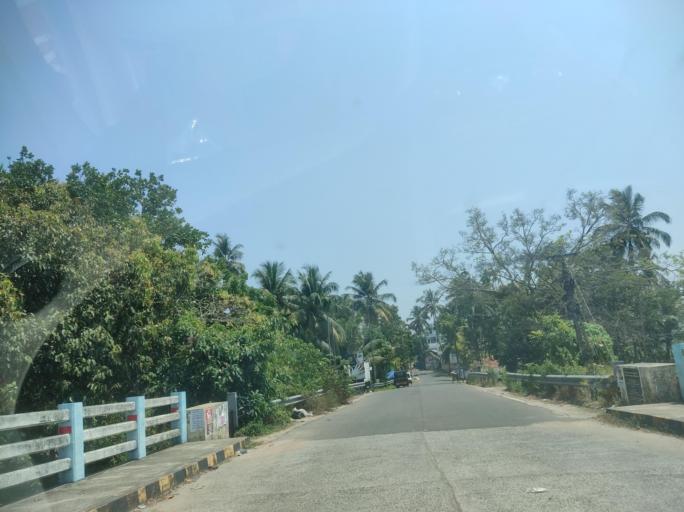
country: IN
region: Kerala
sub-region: Alappuzha
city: Arukutti
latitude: 9.8501
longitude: 76.2945
